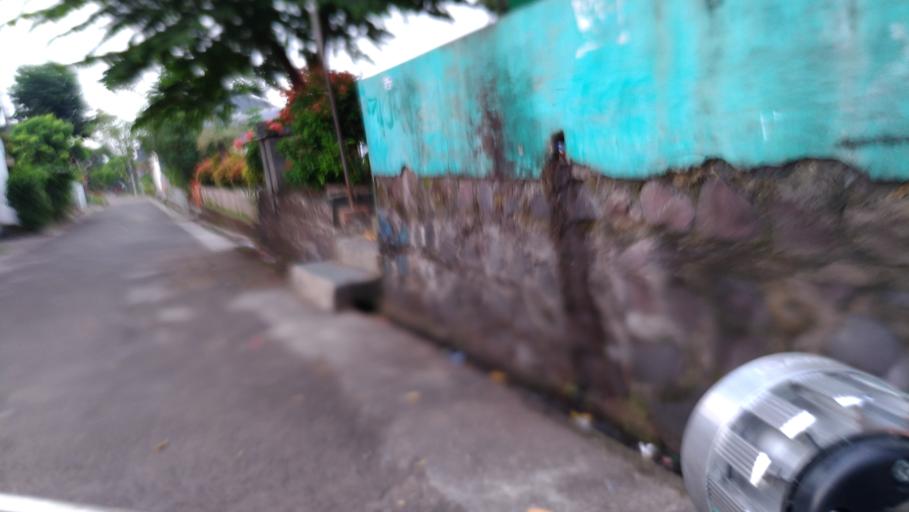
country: ID
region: West Java
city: Depok
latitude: -6.3648
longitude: 106.8656
